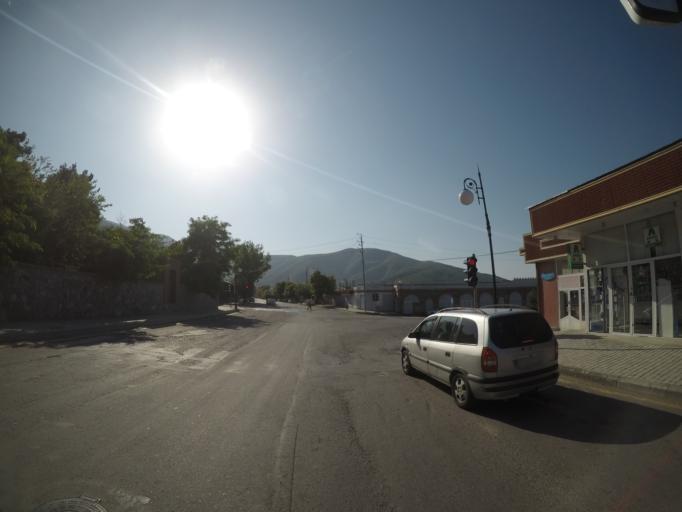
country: AZ
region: Shaki City
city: Sheki
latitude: 41.2064
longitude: 47.1685
